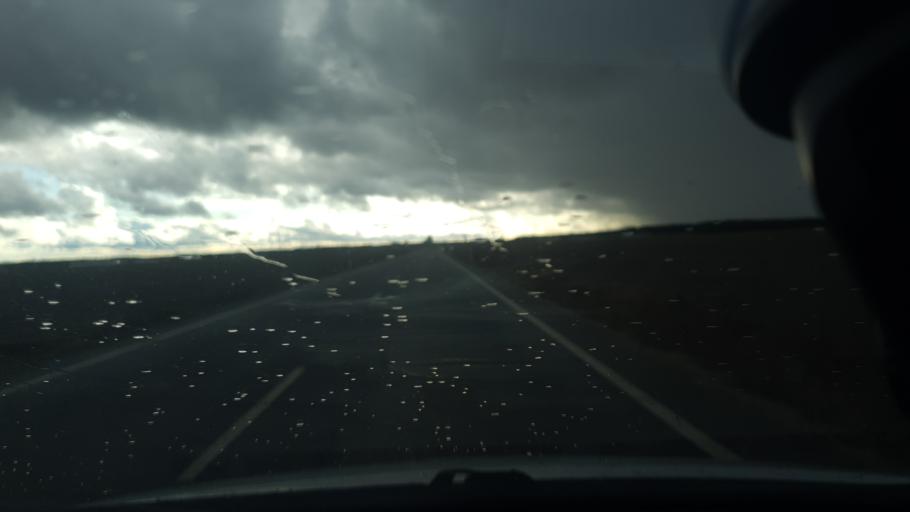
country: ES
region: Castille and Leon
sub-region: Provincia de Segovia
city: Chane
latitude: 41.3081
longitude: -4.3976
